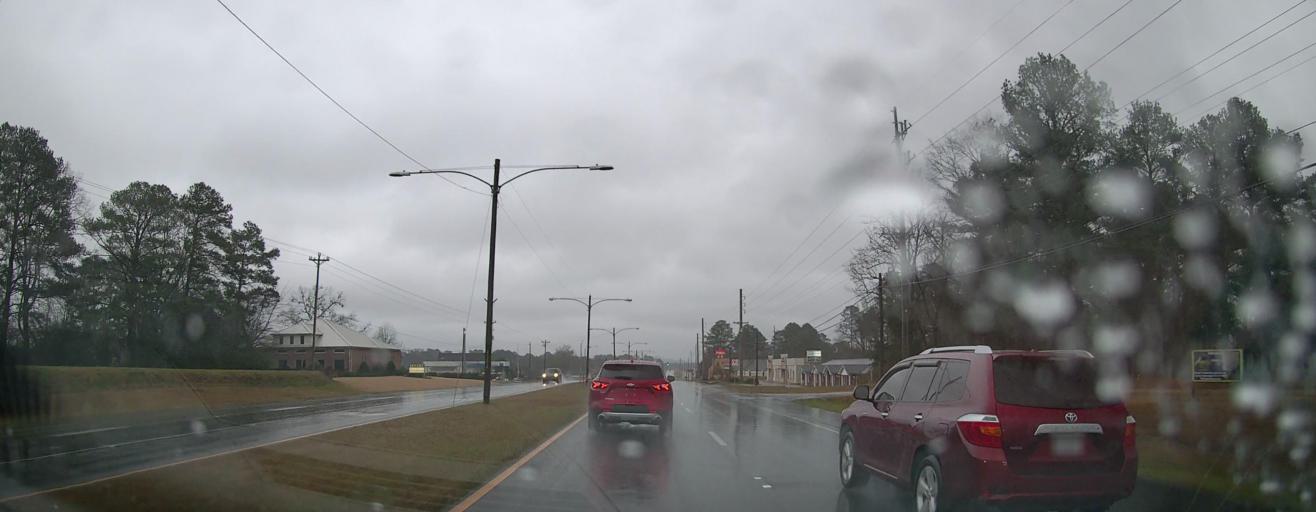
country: US
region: Alabama
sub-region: Morgan County
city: Hartselle
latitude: 34.4312
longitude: -86.9350
